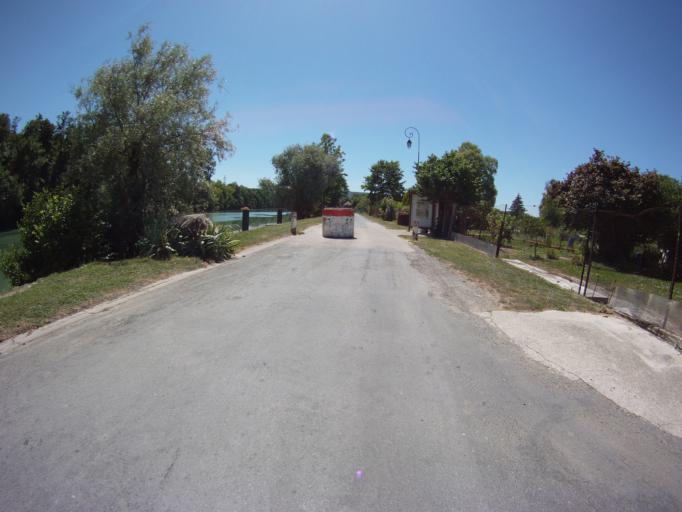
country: FR
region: Champagne-Ardenne
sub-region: Departement de la Marne
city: Mardeuil
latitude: 49.0689
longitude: 3.9229
